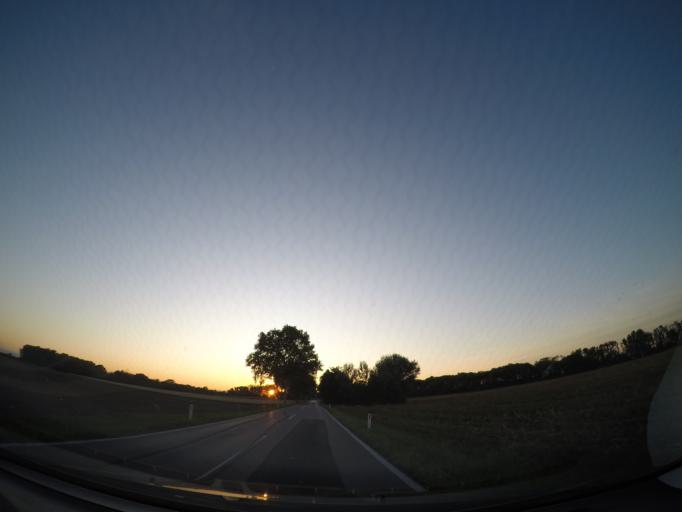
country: AT
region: Lower Austria
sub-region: Politischer Bezirk Baden
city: Mitterndorf an der Fischa
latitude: 47.9622
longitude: 16.4730
